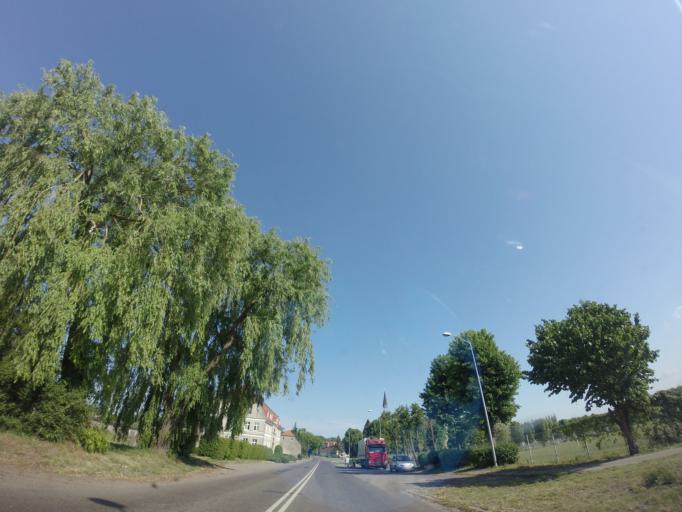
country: PL
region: West Pomeranian Voivodeship
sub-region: Powiat gryfinski
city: Stare Czarnowo
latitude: 53.3026
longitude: 14.8110
